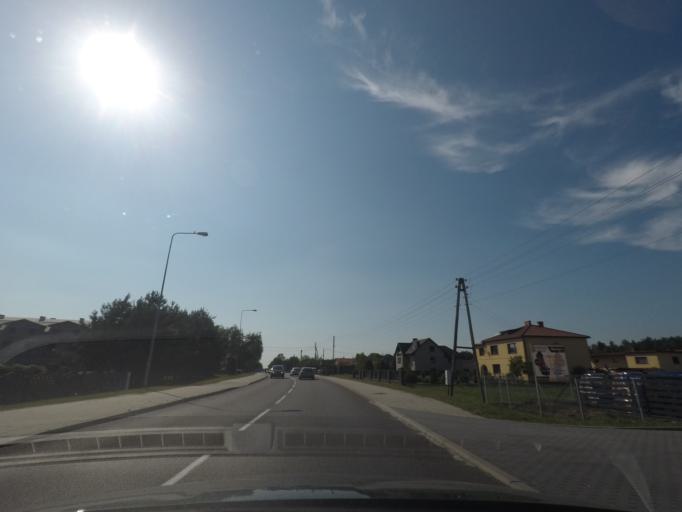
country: PL
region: Silesian Voivodeship
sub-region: Powiat pszczynski
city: Rudziczka
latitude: 50.0380
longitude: 18.7472
